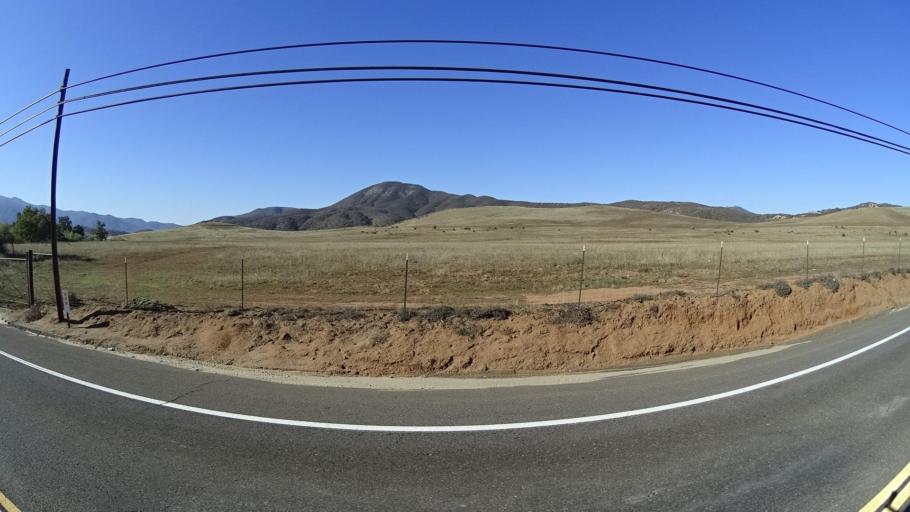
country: US
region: California
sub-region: San Diego County
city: Jamul
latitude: 32.6980
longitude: -116.8618
